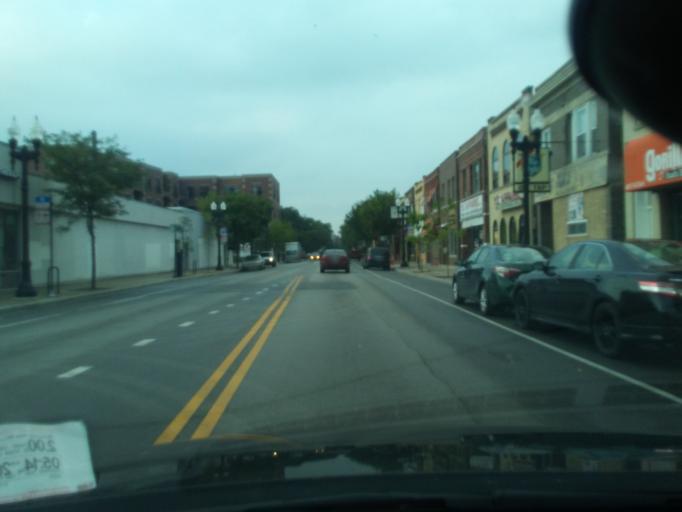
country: US
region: Illinois
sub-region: Cook County
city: Lincolnwood
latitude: 41.9658
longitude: -87.6668
